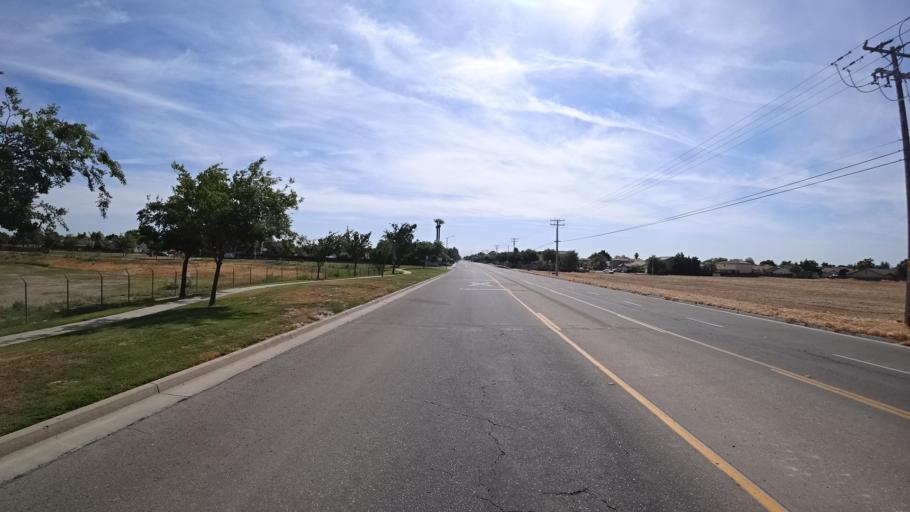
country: US
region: California
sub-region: Kings County
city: Lucerne
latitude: 36.3573
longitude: -119.6633
